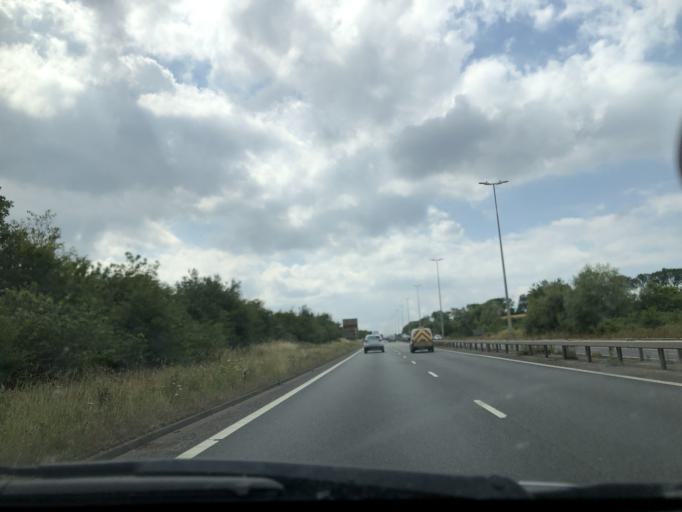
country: GB
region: England
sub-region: Kent
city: Whitstable
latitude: 51.3392
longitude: 1.0375
